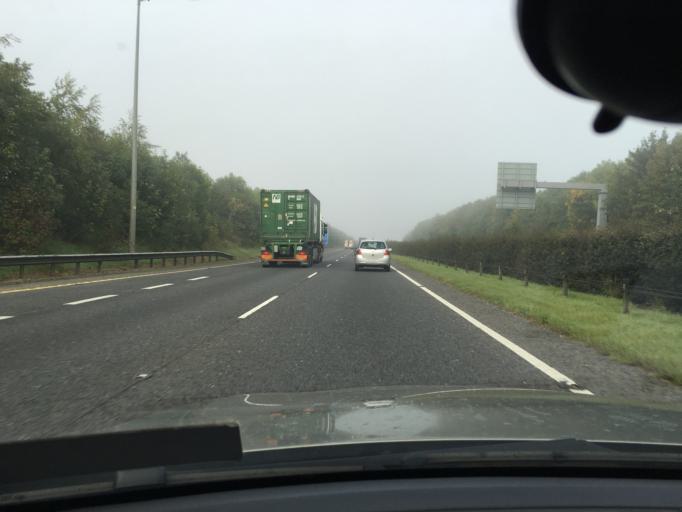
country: IE
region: Leinster
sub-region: Kildare
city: Celbridge
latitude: 53.3605
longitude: -6.5393
